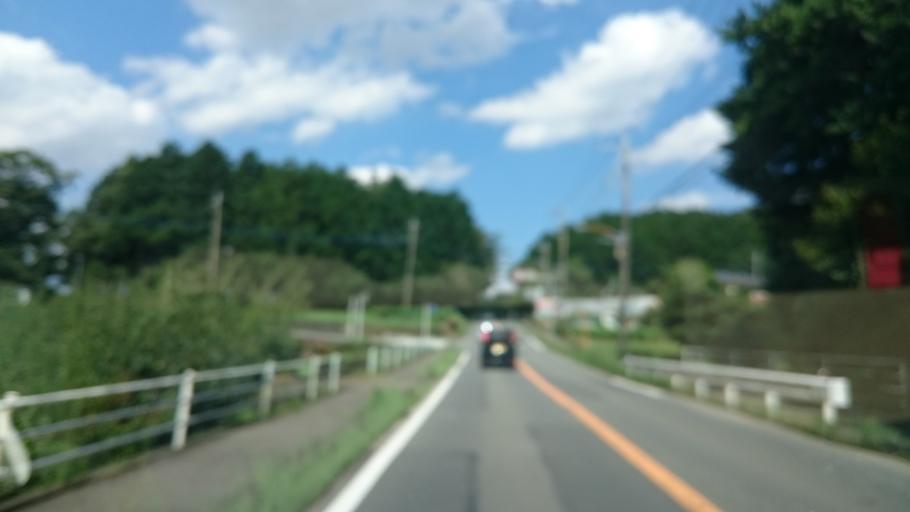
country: JP
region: Shizuoka
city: Mishima
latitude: 35.2062
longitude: 138.9253
